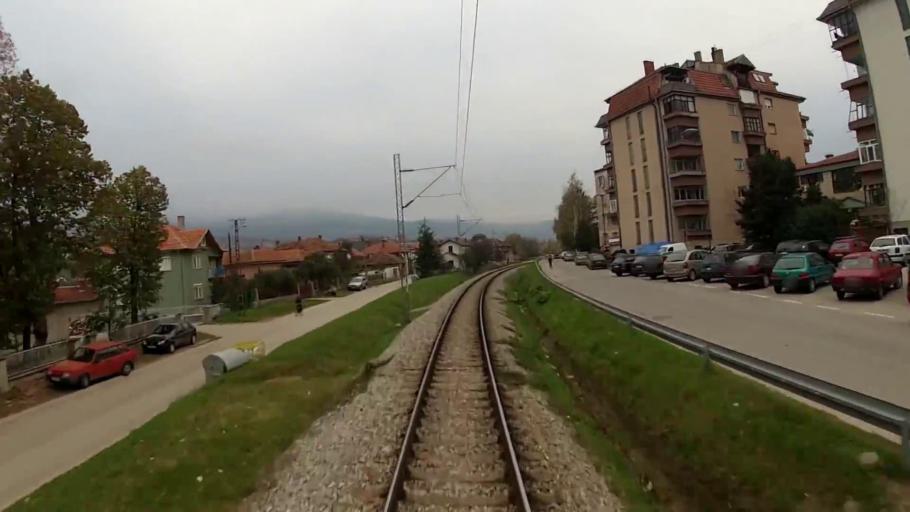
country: RS
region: Central Serbia
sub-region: Pirotski Okrug
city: Dimitrovgrad
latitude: 43.0161
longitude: 22.7874
